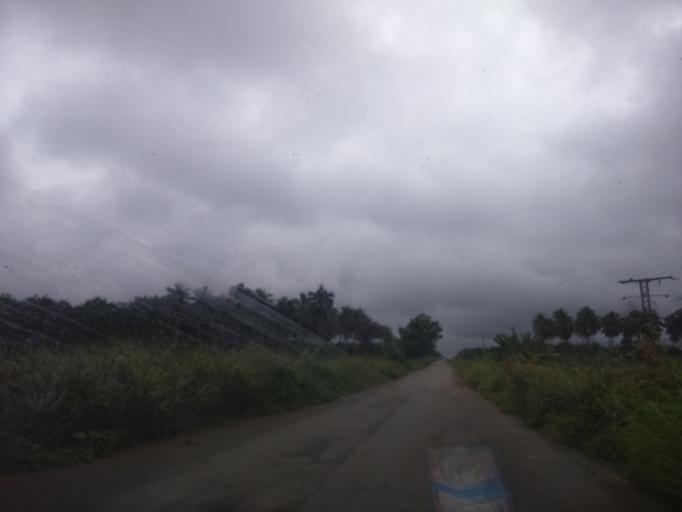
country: CI
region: Sud-Comoe
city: Bonoua
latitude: 5.2884
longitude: -3.4573
